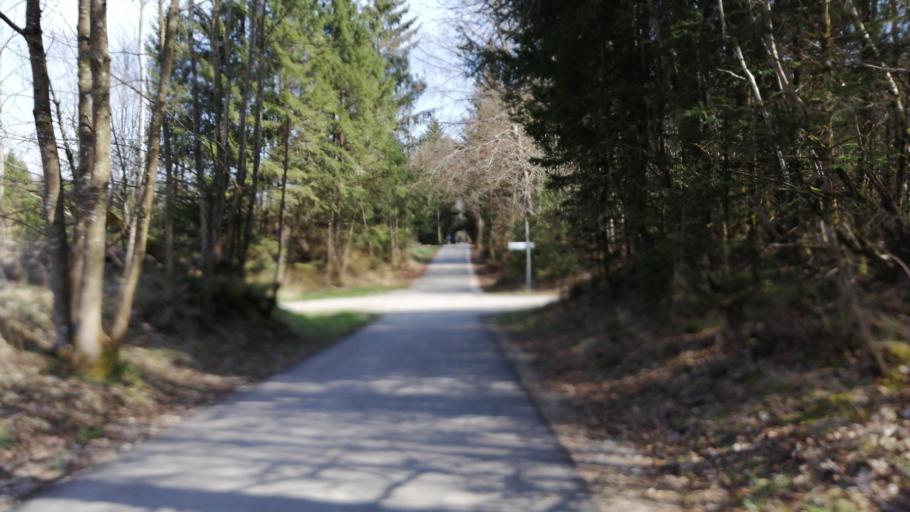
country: DE
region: Bavaria
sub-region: Upper Bavaria
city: Sauerlach
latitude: 47.9896
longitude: 11.6268
